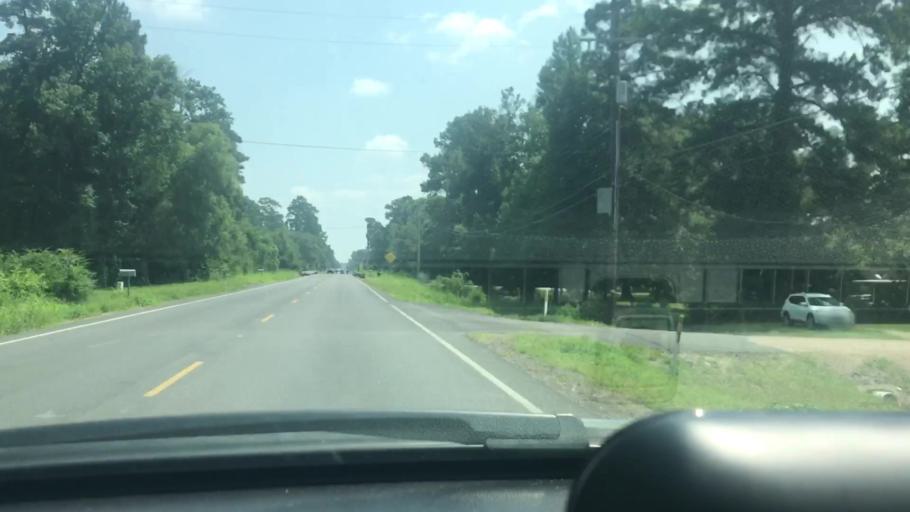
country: US
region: Louisiana
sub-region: Livingston Parish
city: Walker
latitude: 30.4848
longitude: -90.8948
